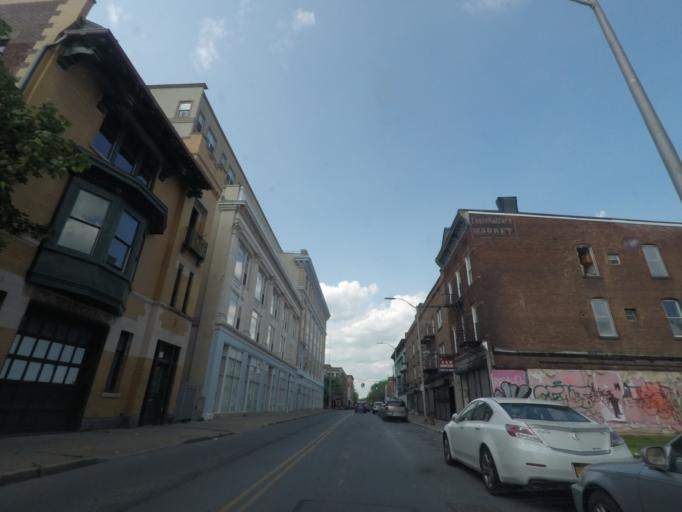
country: US
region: New York
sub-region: Dutchess County
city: Poughkeepsie
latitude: 41.7020
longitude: -73.9260
